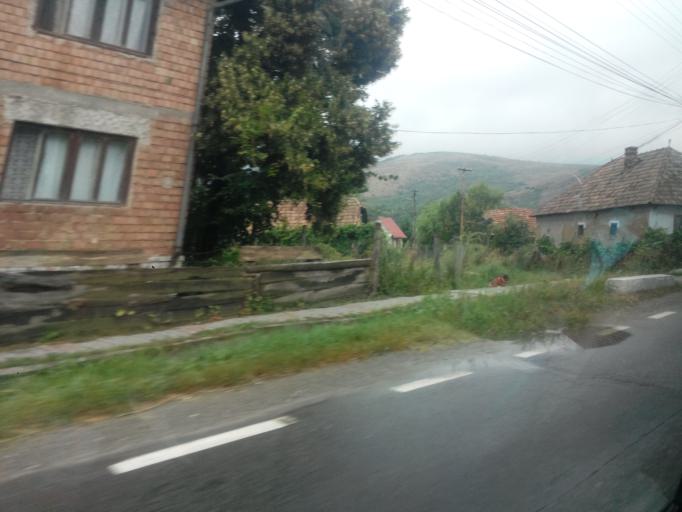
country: RO
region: Cluj
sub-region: Comuna Moldovenesti
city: Moldovenesti
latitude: 46.5243
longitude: 23.6945
